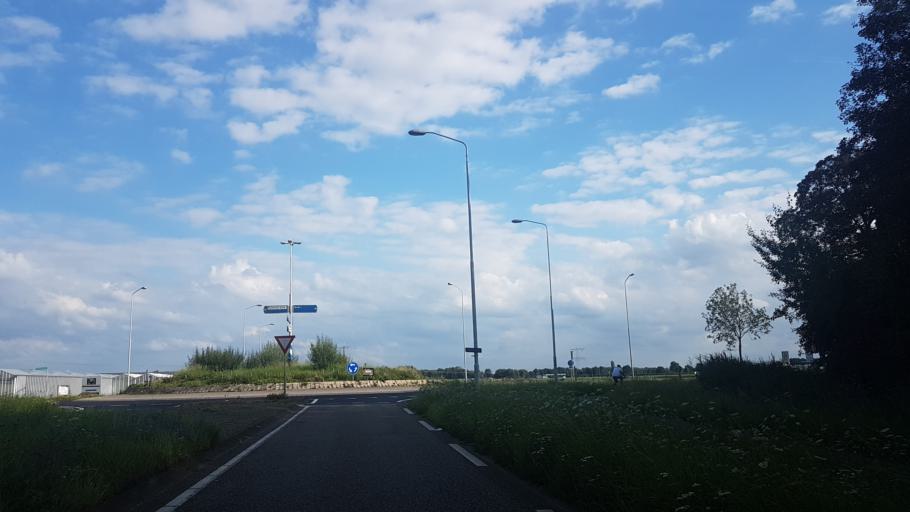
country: NL
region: North Brabant
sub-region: Gemeente Made en Drimmelen
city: Made
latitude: 51.6811
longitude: 4.8176
